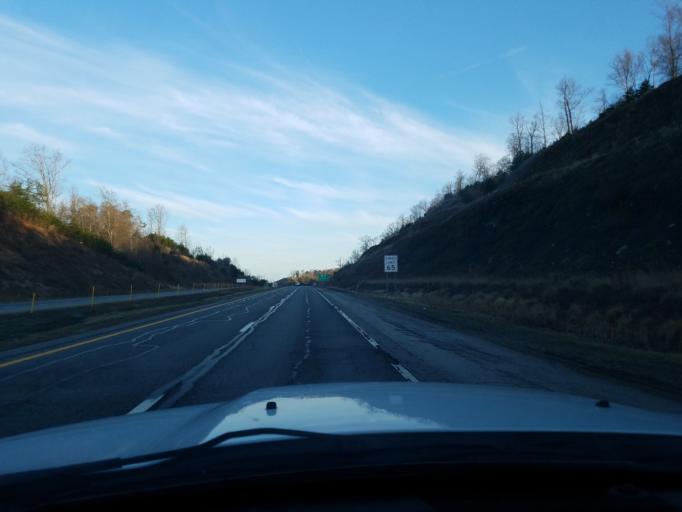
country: US
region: West Virginia
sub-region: Putnam County
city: Teays Valley
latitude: 38.4642
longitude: -81.9075
